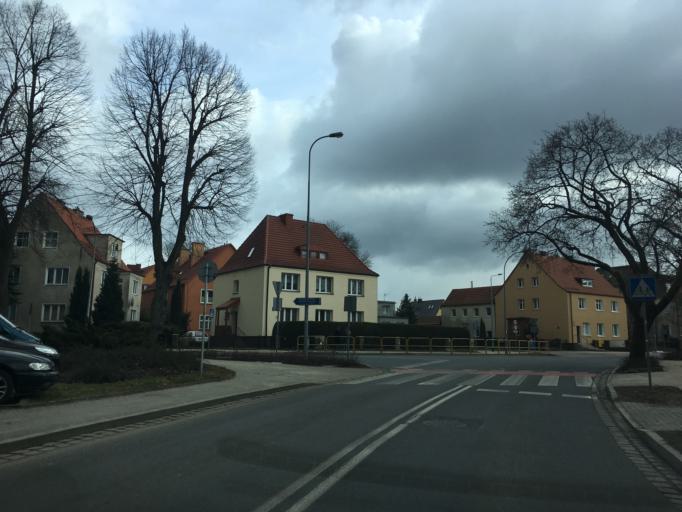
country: PL
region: Pomeranian Voivodeship
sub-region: Slupsk
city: Slupsk
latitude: 54.4596
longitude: 17.0425
